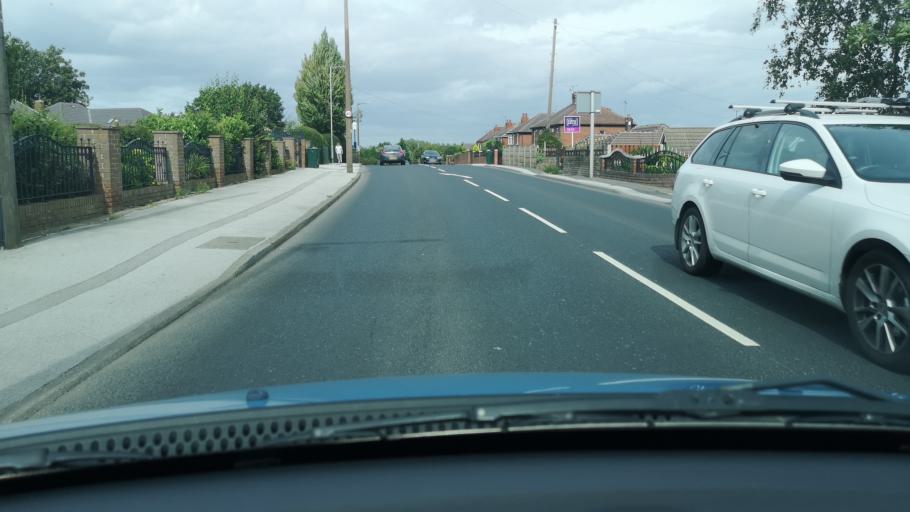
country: GB
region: England
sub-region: Barnsley
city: Cudworth
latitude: 53.5687
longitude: -1.4307
